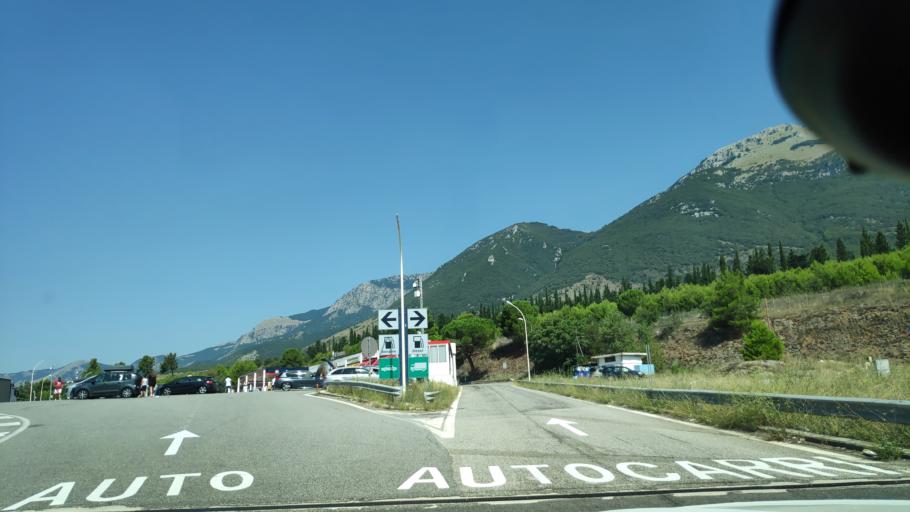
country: IT
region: Calabria
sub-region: Provincia di Cosenza
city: Frascineto
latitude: 39.8423
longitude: 16.2463
